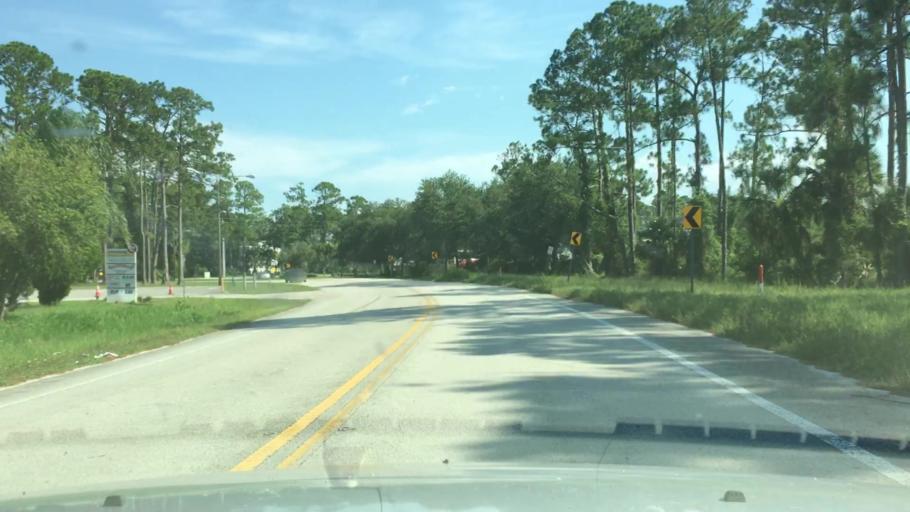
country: US
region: Florida
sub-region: Volusia County
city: Daytona Beach
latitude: 29.1908
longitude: -81.0794
